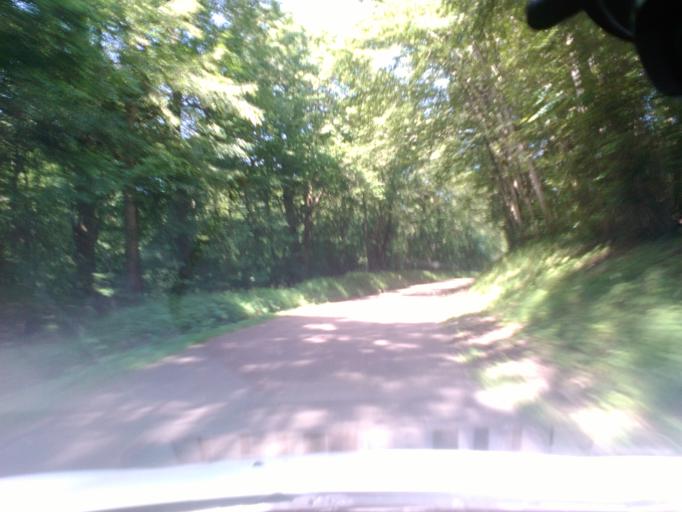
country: FR
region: Lorraine
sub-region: Departement des Vosges
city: Liffol-le-Grand
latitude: 48.2972
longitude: 5.4695
